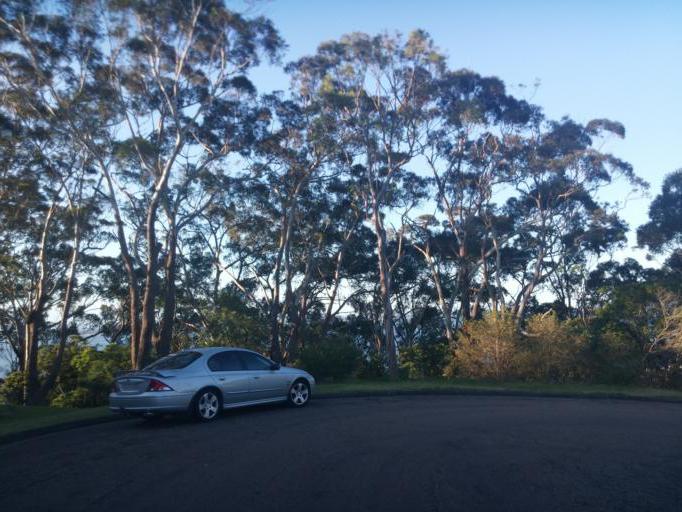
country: AU
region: New South Wales
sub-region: Port Stephens Shire
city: Nelson Bay
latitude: -32.7193
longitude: 152.1417
